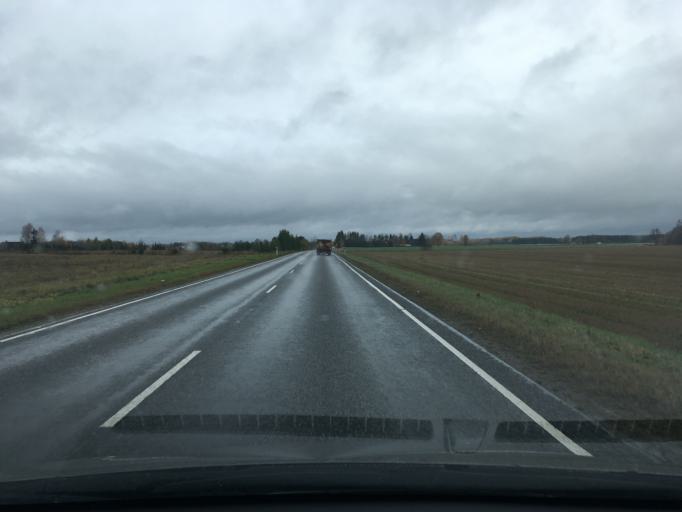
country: EE
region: Jogevamaa
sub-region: Tabivere vald
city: Tabivere
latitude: 58.4647
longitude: 26.6301
